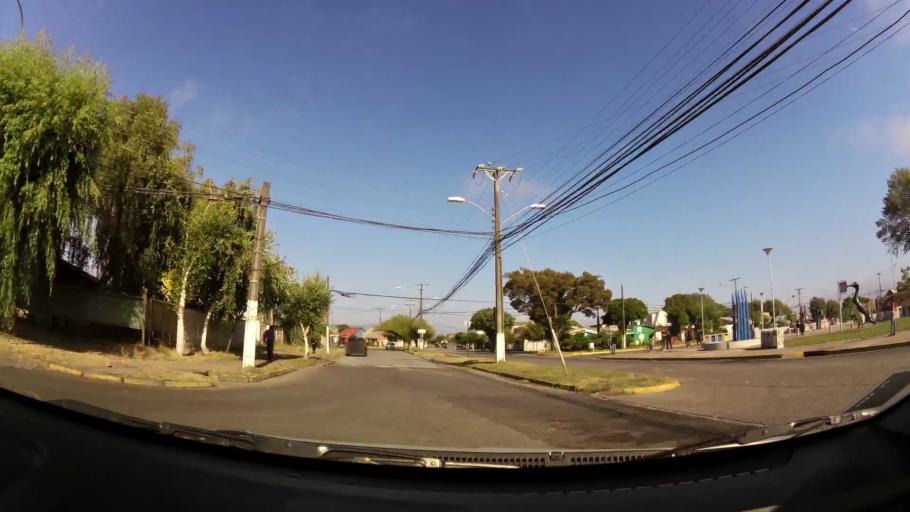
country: CL
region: Biobio
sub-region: Provincia de Concepcion
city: Concepcion
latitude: -36.8000
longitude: -73.0942
